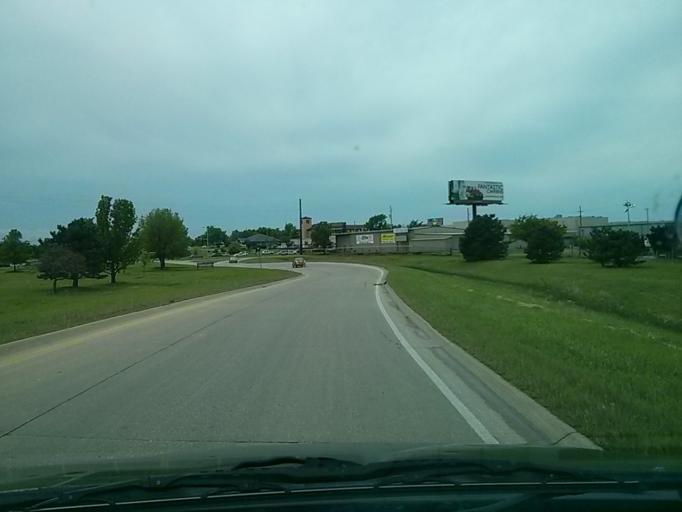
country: US
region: Oklahoma
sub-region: Tulsa County
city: Broken Arrow
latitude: 36.0773
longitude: -95.8600
